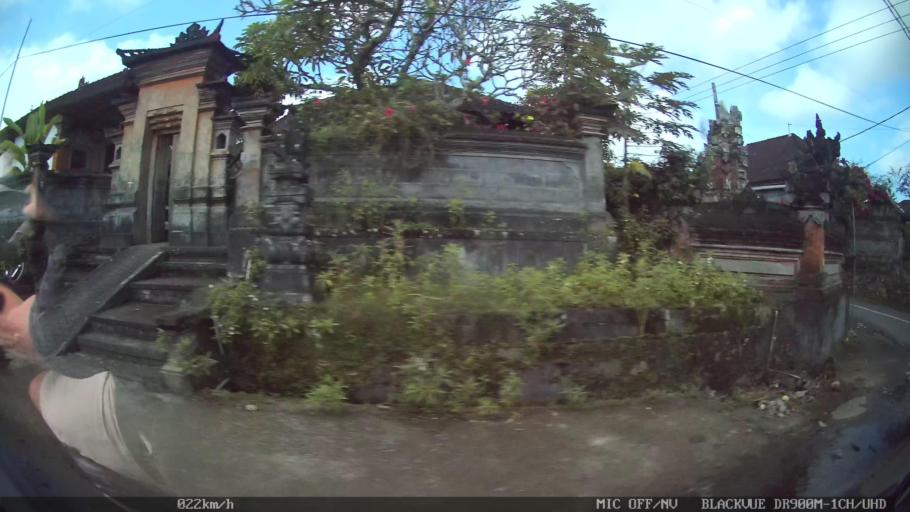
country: ID
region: Bali
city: Banjar Pesalakan
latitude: -8.5151
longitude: 115.3061
